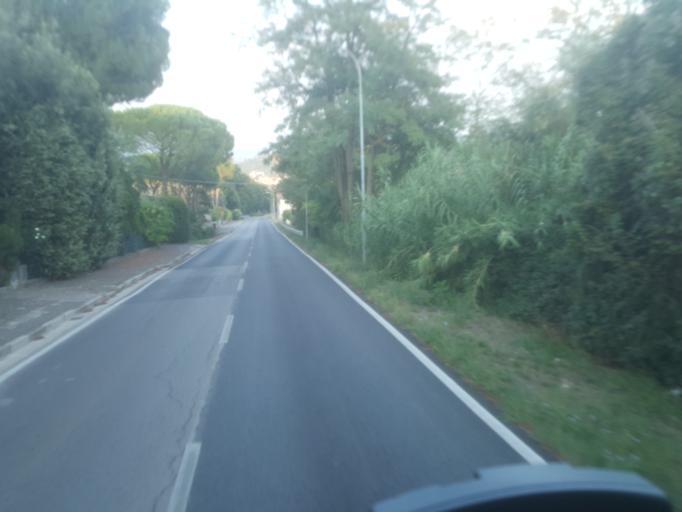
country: IT
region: Tuscany
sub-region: Province of Florence
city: Certaldo
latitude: 43.5449
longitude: 11.0188
